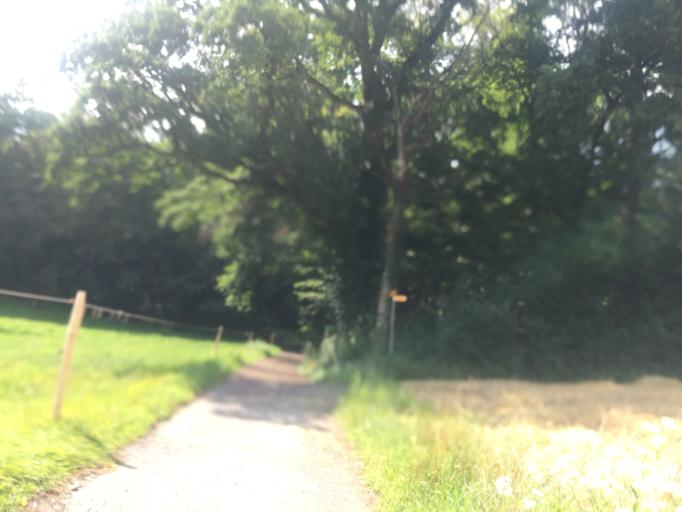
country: CH
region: Bern
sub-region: Bern-Mittelland District
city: Rubigen
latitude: 46.9065
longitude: 7.5265
